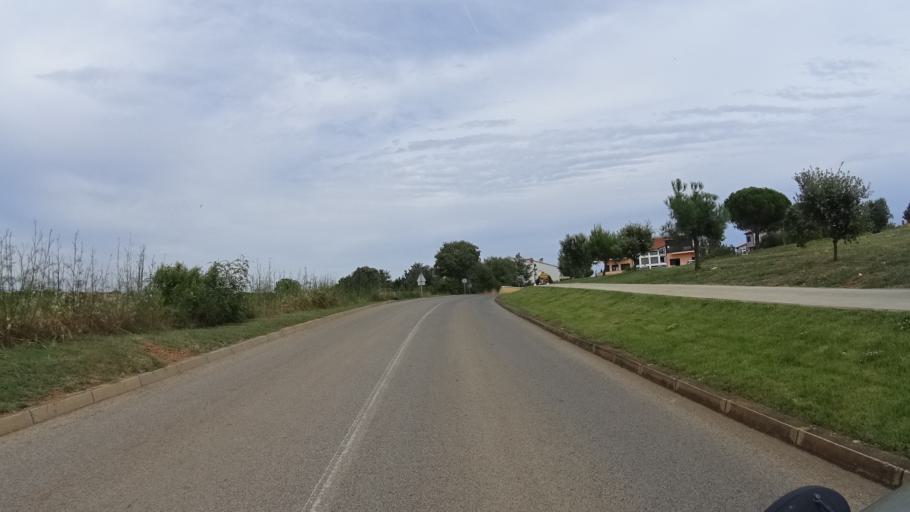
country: HR
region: Istarska
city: Medulin
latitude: 44.8255
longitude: 13.8912
